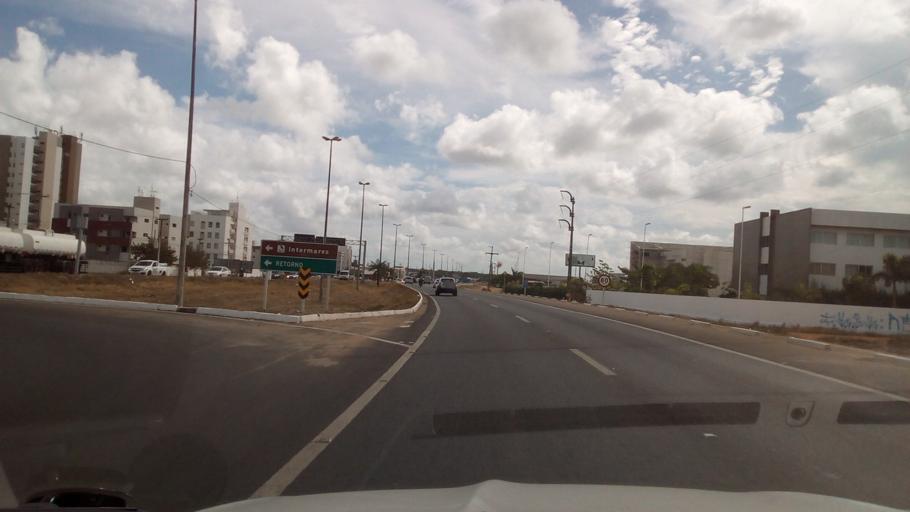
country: BR
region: Paraiba
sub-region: Cabedelo
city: Cabedelo
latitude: -7.0441
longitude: -34.8470
